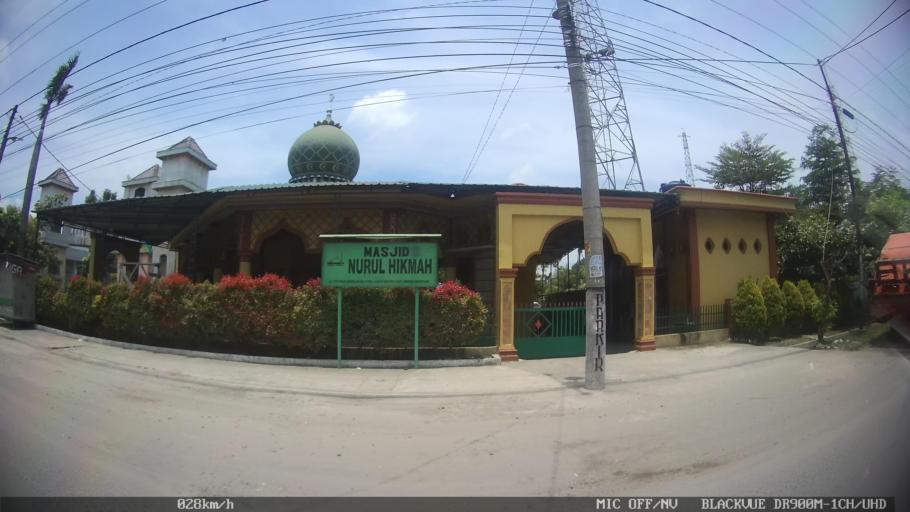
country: ID
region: North Sumatra
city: Labuhan Deli
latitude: 3.7206
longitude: 98.6711
